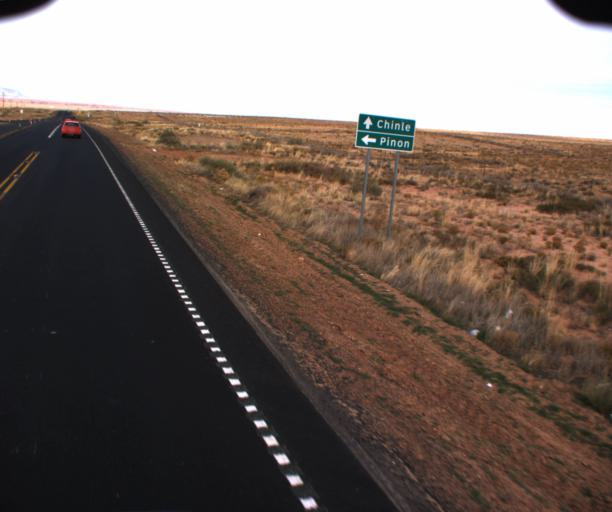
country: US
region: Arizona
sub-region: Apache County
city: Chinle
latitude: 36.0927
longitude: -109.6242
